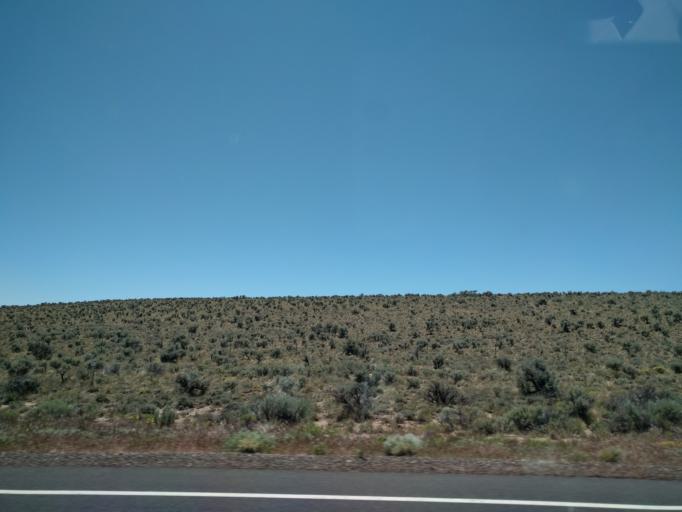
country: US
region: Oregon
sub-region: Harney County
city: Hines
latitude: 43.5801
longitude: -119.9499
